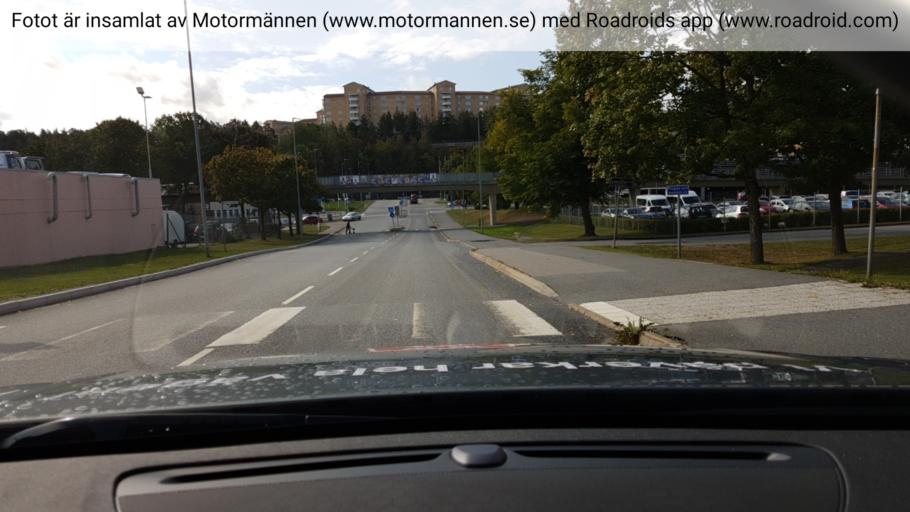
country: SE
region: Stockholm
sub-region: Botkyrka Kommun
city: Eriksberg
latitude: 59.2460
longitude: 17.8295
